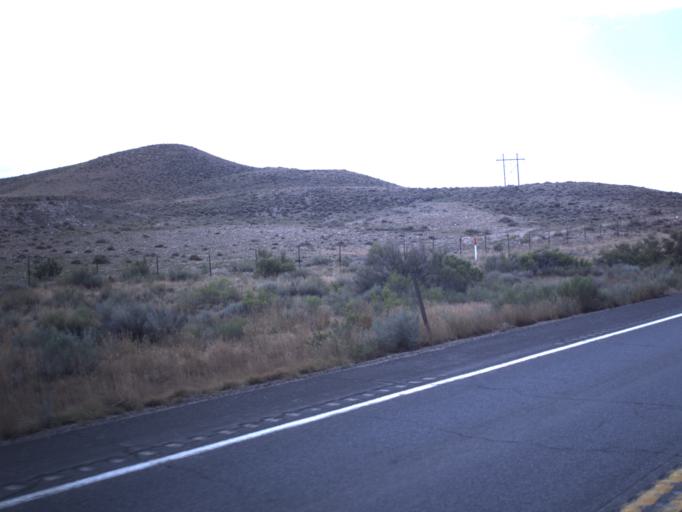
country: US
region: Utah
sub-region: Duchesne County
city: Duchesne
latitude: 40.1529
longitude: -110.2390
